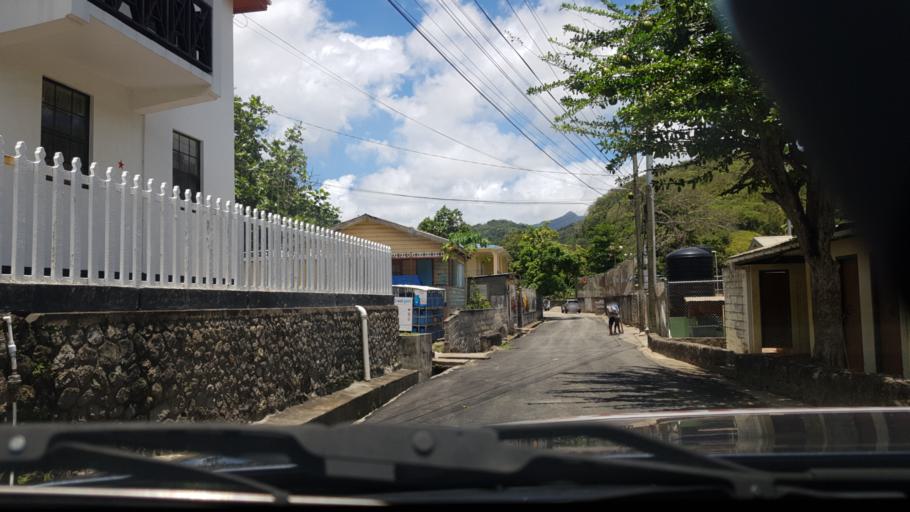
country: LC
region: Anse-la-Raye
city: Canaries
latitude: 13.9041
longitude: -61.0667
